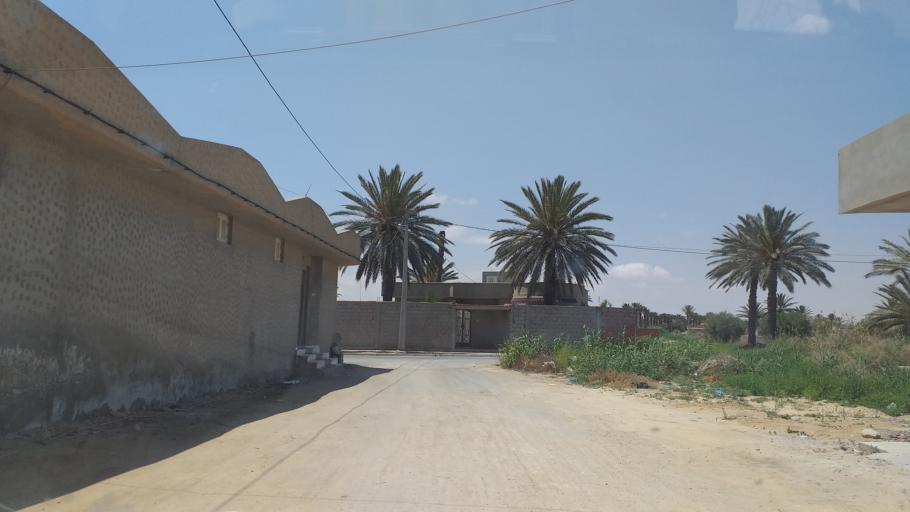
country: TN
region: Qabis
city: Gabes
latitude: 33.9442
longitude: 10.0560
